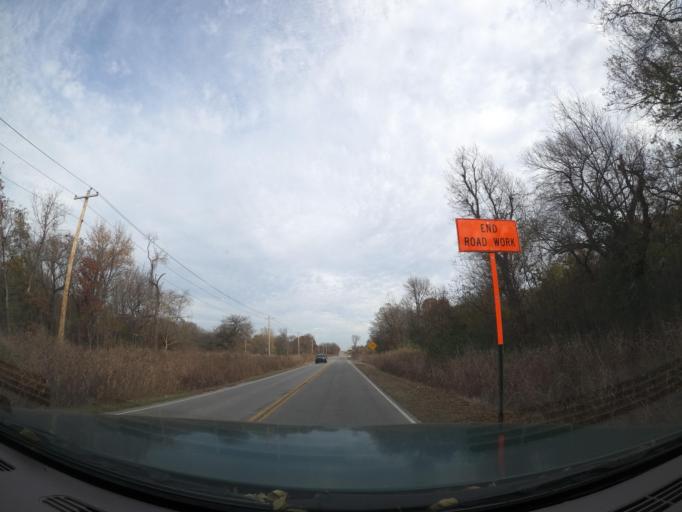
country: US
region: Oklahoma
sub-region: Tulsa County
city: Turley
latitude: 36.2060
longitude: -95.9714
